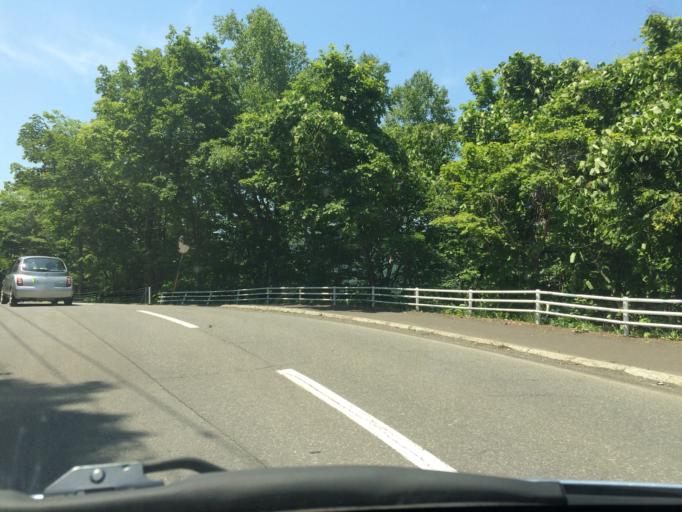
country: JP
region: Hokkaido
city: Sapporo
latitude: 42.9640
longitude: 141.2815
